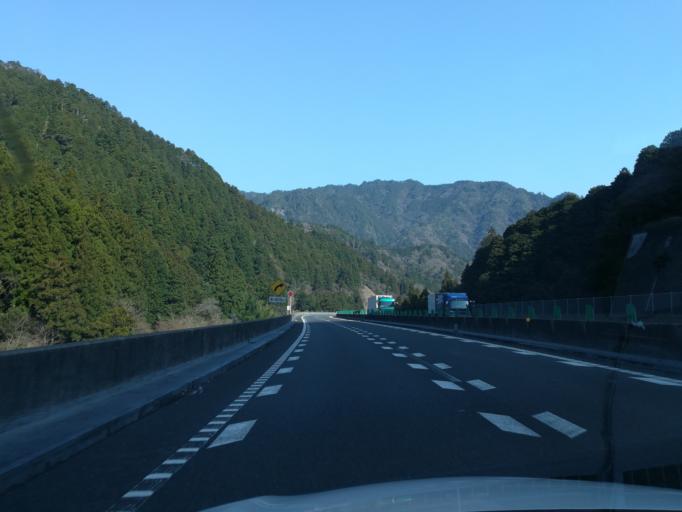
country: JP
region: Ehime
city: Kawanoecho
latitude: 33.9055
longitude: 133.6308
